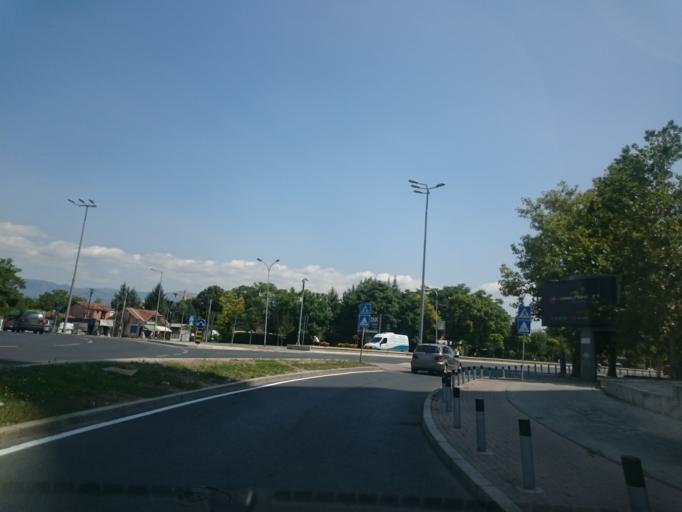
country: MK
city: Krushopek
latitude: 42.0083
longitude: 21.3685
